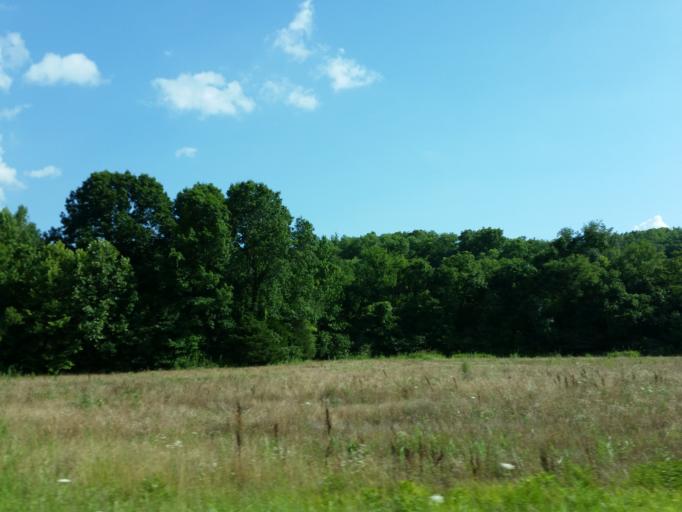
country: US
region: Tennessee
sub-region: Perry County
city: Linden
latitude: 35.6333
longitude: -87.7744
